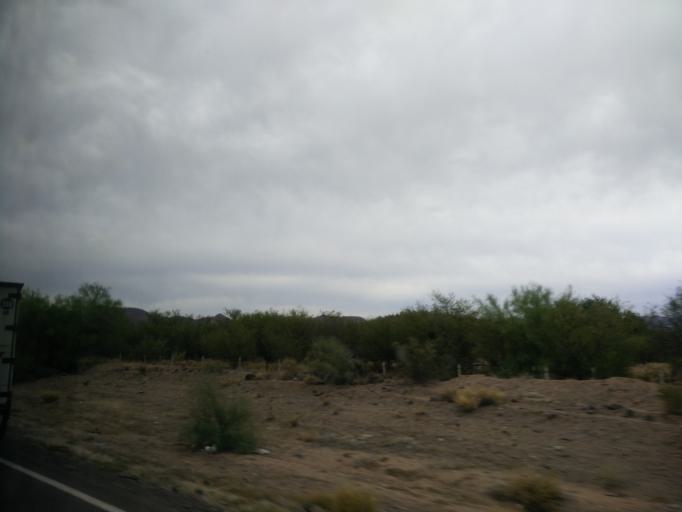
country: MX
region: Sonora
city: Hermosillo
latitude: 28.9171
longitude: -110.9521
